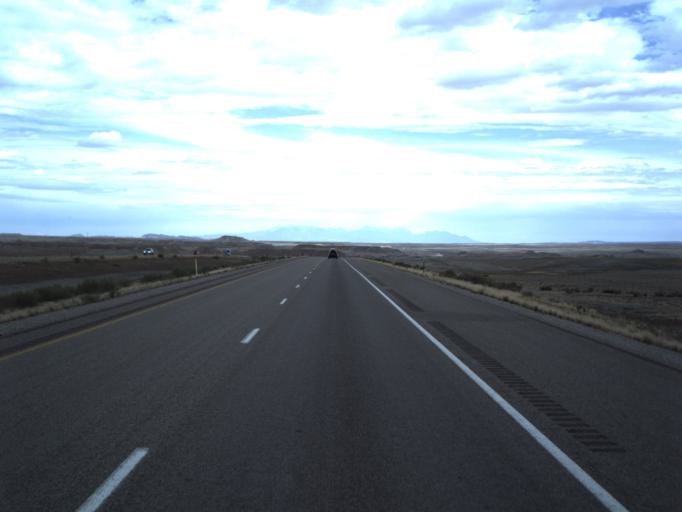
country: US
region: Utah
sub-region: Grand County
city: Moab
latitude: 38.9529
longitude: -110.0523
